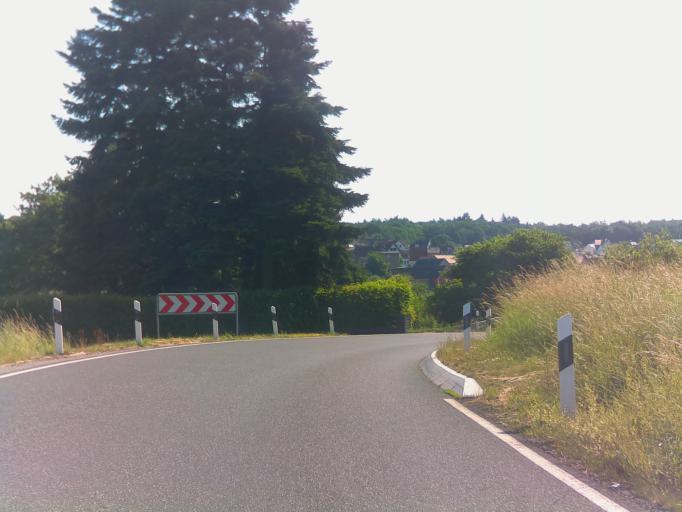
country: DE
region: Hesse
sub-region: Regierungsbezirk Giessen
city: Rabenau
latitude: 50.6565
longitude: 8.8431
